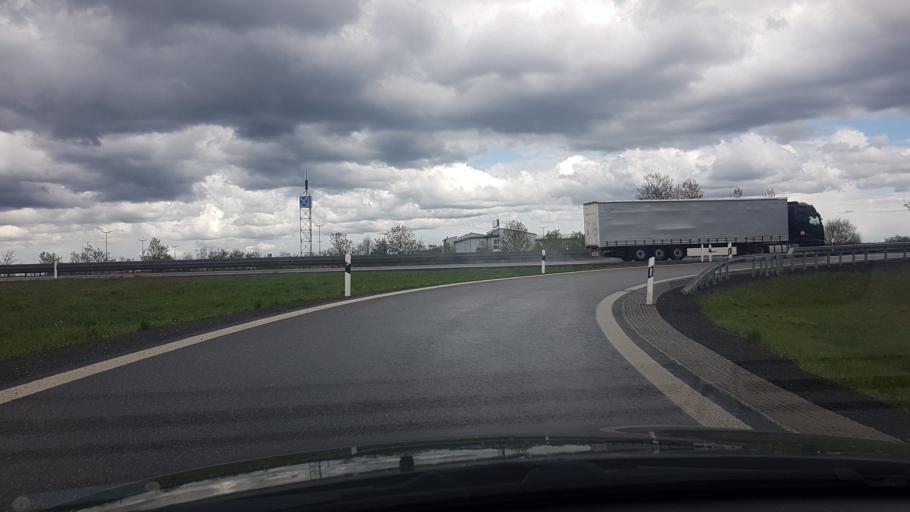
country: DE
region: Bavaria
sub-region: Upper Palatinate
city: Mitterteich
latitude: 49.9366
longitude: 12.2239
